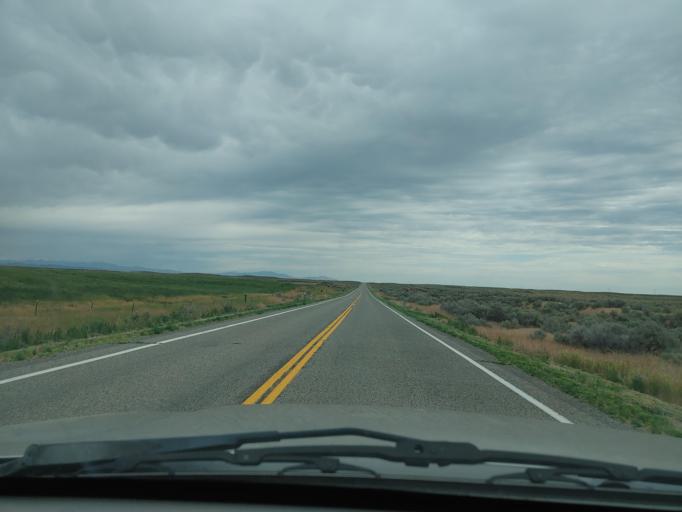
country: US
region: Idaho
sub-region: Lincoln County
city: Shoshone
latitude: 43.0648
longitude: -114.1209
